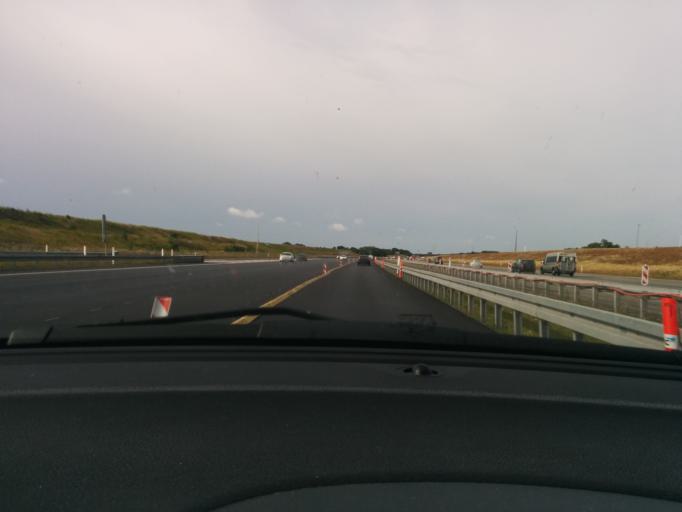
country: DK
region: Zealand
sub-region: Greve Kommune
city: Greve
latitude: 55.5807
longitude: 12.2576
